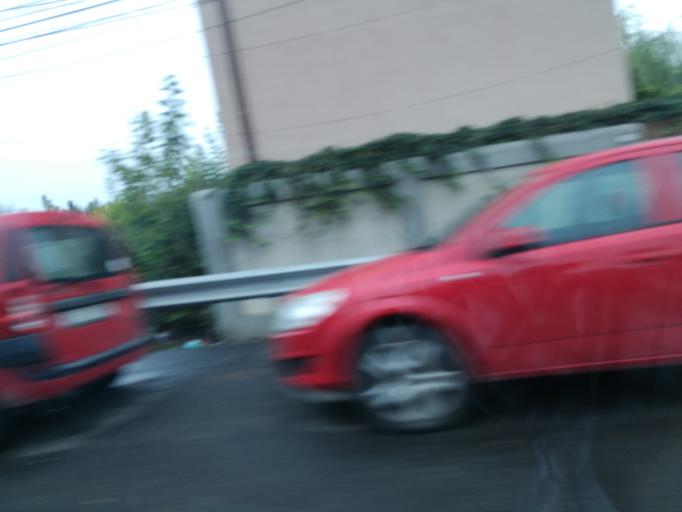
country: RO
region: Galati
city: Galati
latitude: 45.4664
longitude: 28.0352
